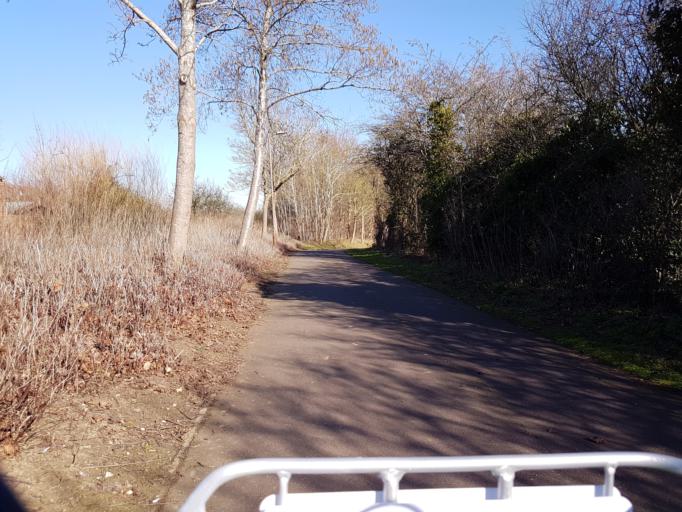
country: GB
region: England
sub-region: Buckinghamshire
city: Bletchley
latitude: 52.0108
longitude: -0.7541
